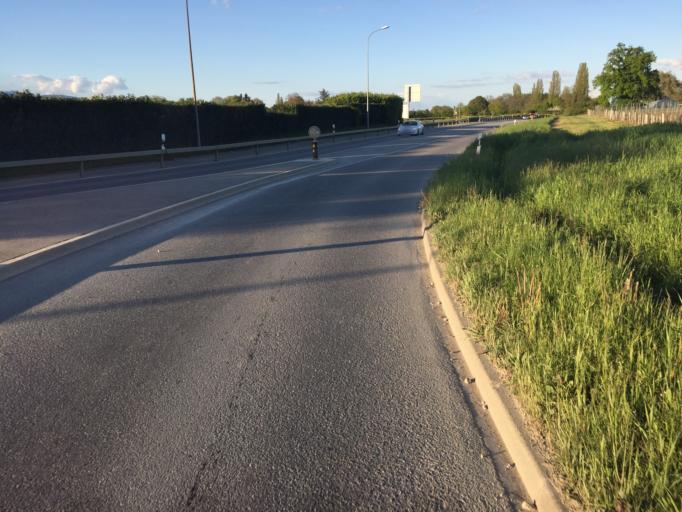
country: CH
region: Geneva
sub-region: Geneva
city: Aire-la-Ville
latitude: 46.1707
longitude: 6.0386
